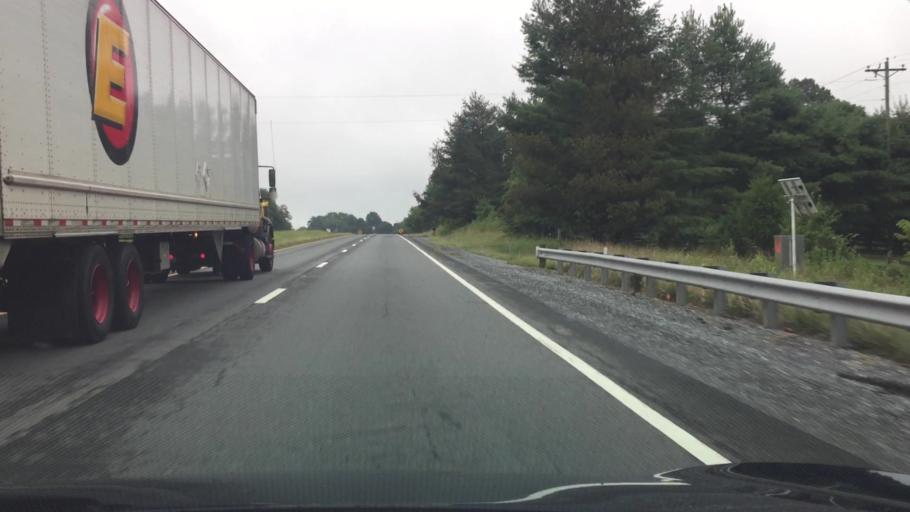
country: US
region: Virginia
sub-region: Bedford County
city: Forest
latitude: 37.3013
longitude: -79.3804
